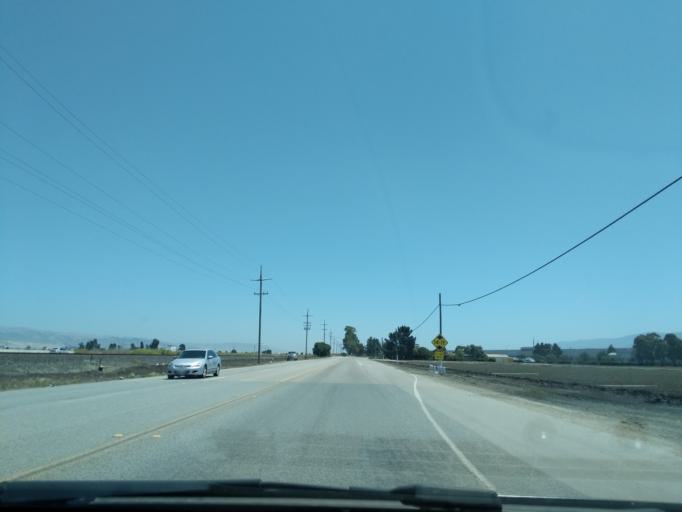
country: US
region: California
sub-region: Monterey County
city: Salinas
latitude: 36.6317
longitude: -121.5942
